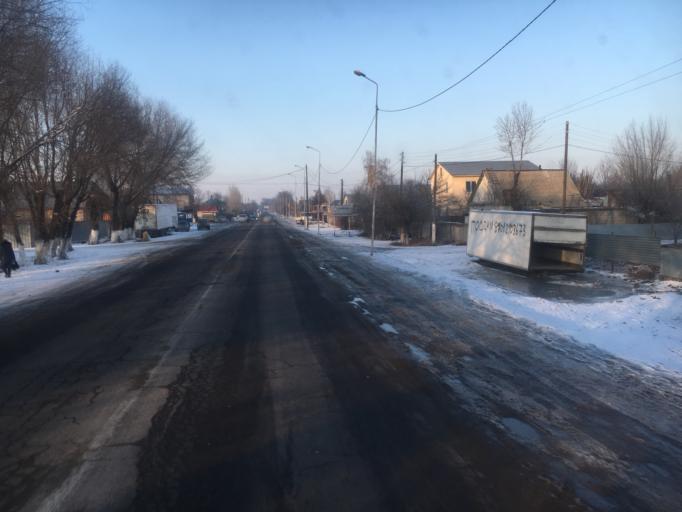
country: KZ
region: Almaty Oblysy
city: Burunday
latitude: 43.3682
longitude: 76.6414
